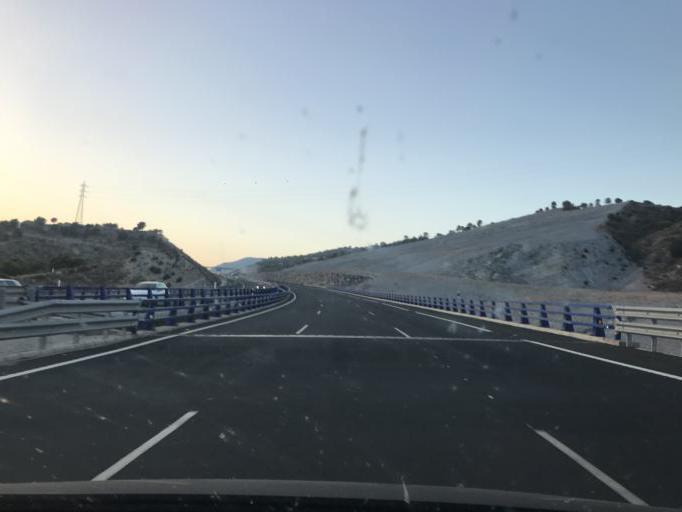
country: ES
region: Andalusia
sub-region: Provincia de Granada
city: Motril
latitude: 36.7707
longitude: -3.4872
